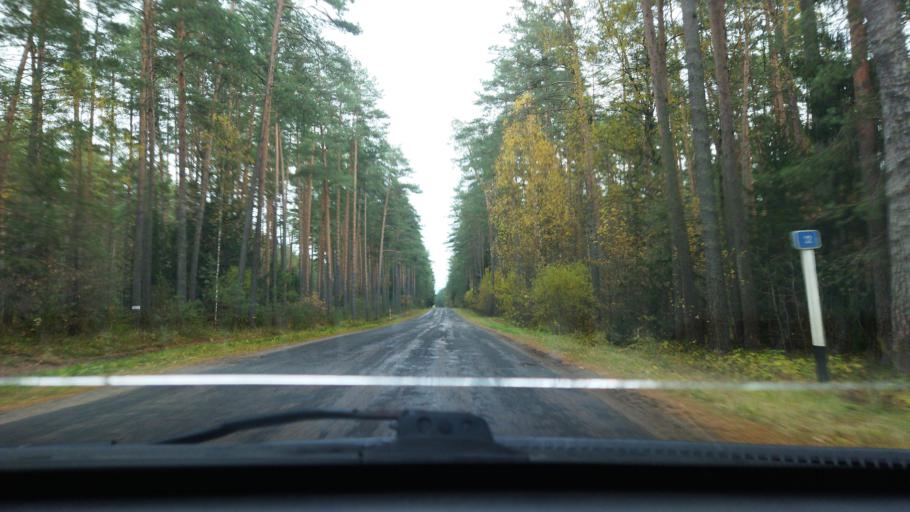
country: BY
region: Minsk
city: Svir
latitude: 54.8115
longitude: 26.2071
